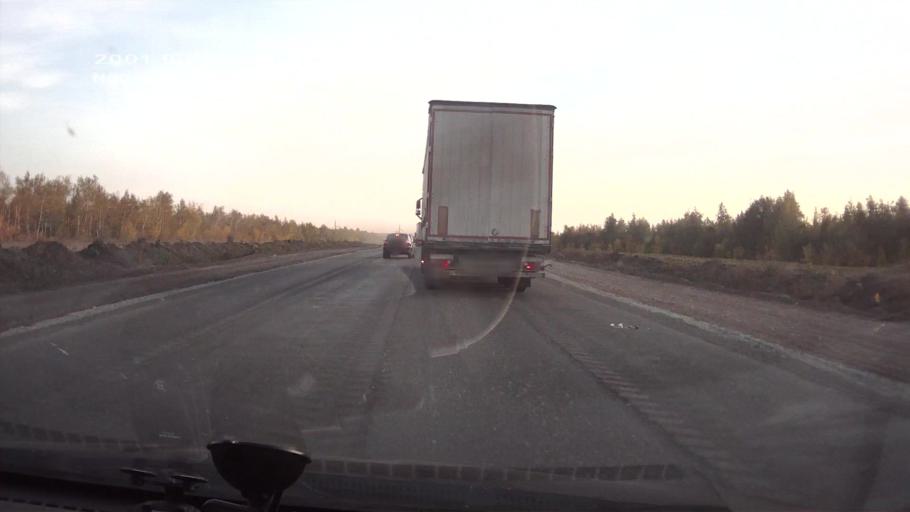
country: RU
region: Saratov
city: Kamenskiy
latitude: 50.9297
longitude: 45.5998
